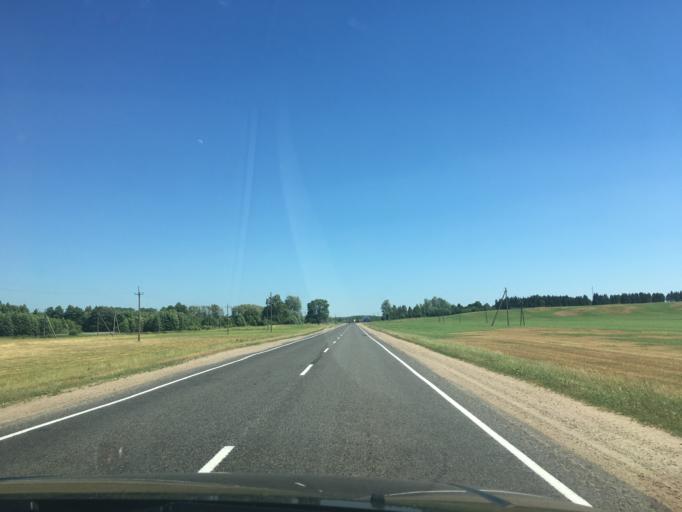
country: BY
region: Grodnenskaya
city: Hal'shany
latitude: 54.2567
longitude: 25.9981
